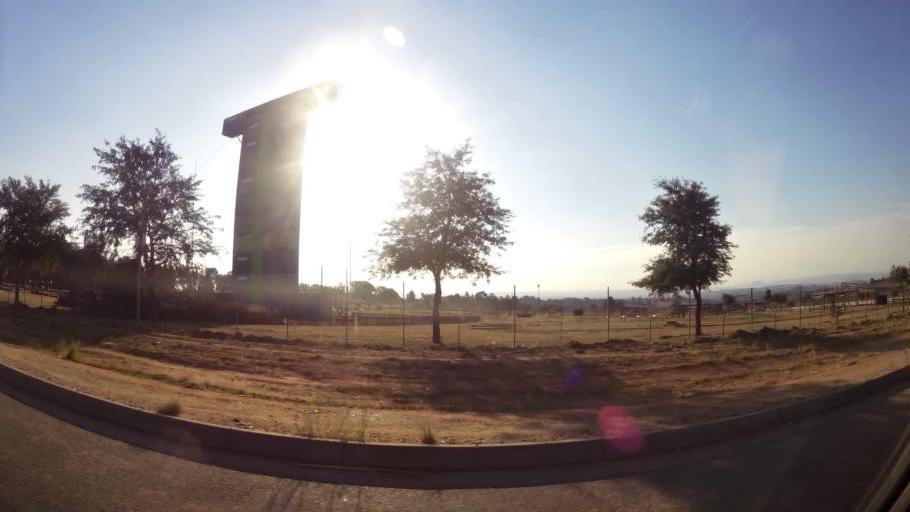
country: ZA
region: Gauteng
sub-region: West Rand District Municipality
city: Muldersdriseloop
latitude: -26.0000
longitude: 27.9223
